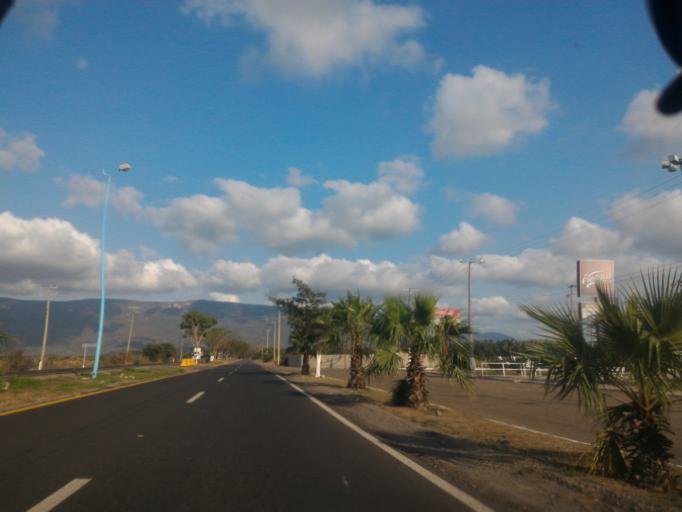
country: MX
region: Colima
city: Tecoman
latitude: 18.9437
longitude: -103.8875
